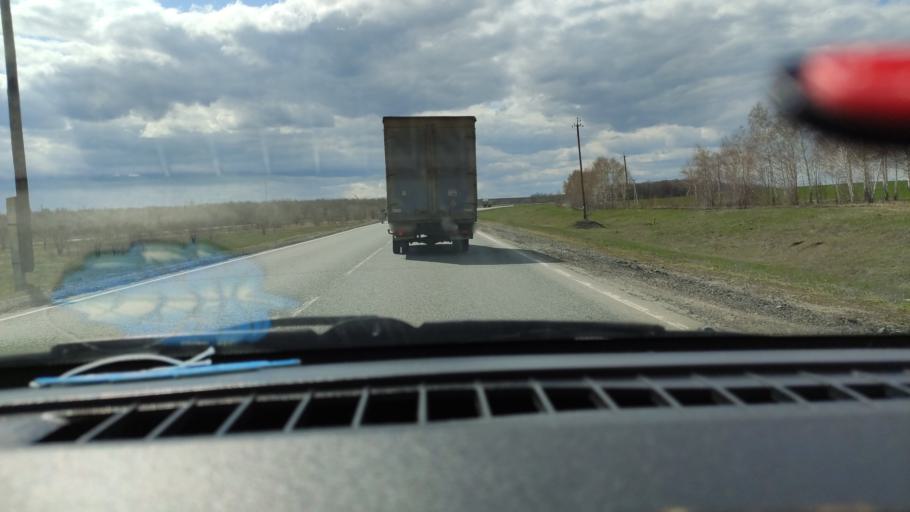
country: RU
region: Saratov
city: Balakovo
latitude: 52.1099
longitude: 47.7473
